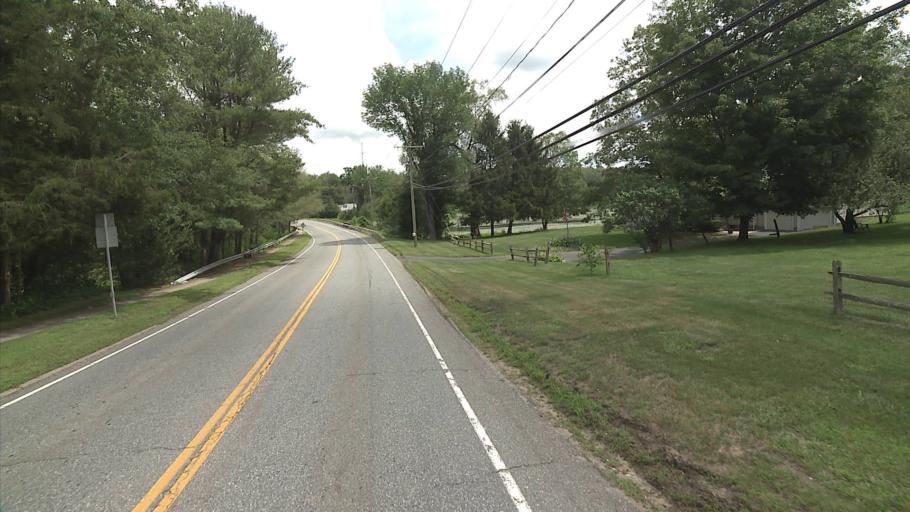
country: US
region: Connecticut
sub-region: Middlesex County
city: Deep River Center
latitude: 41.3813
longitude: -72.4427
